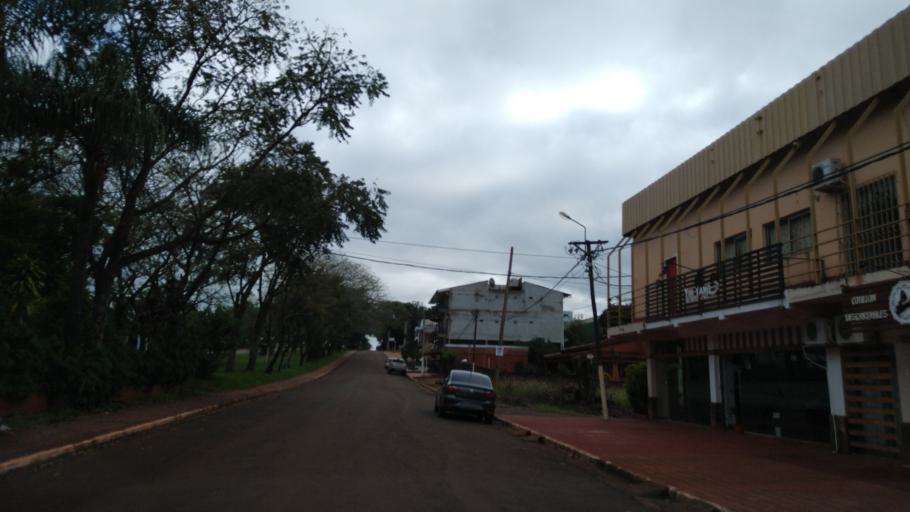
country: AR
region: Misiones
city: Jardin America
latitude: -27.0440
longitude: -55.2371
